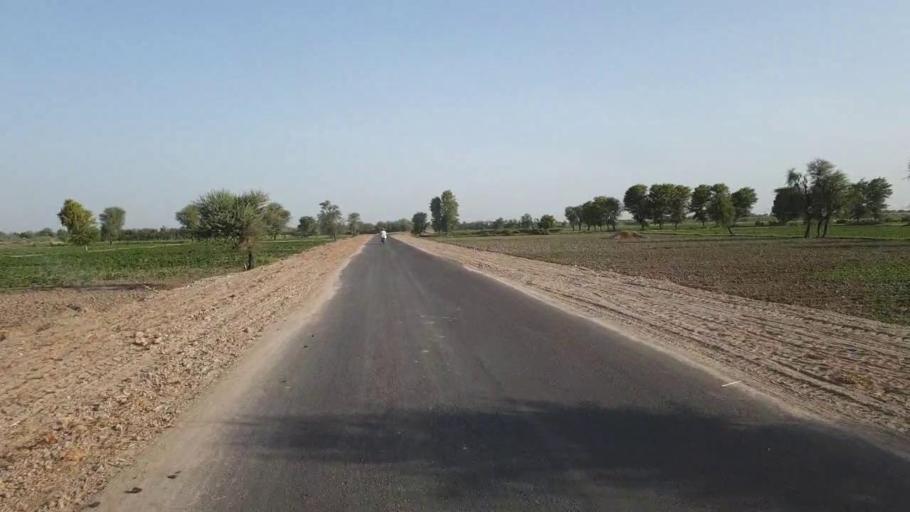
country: PK
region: Sindh
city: Jam Sahib
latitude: 26.3412
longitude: 68.5727
